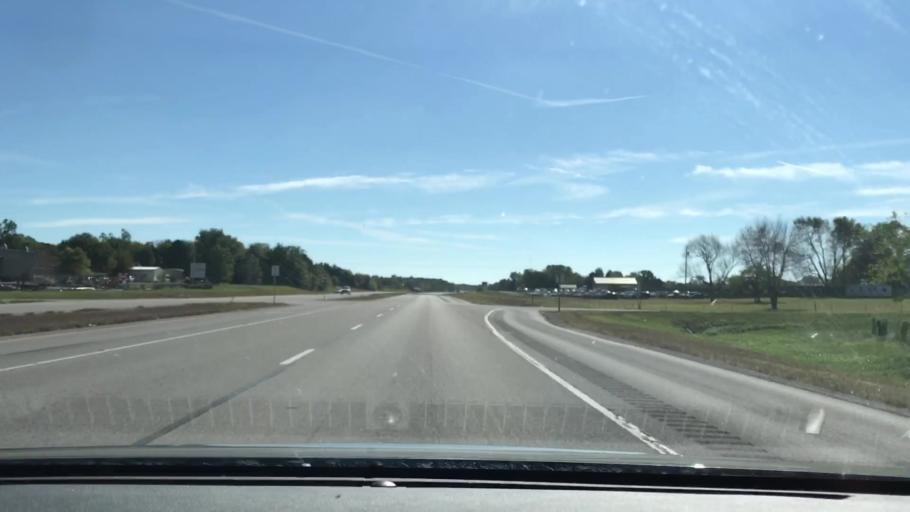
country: US
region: Kentucky
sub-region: Todd County
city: Elkton
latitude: 36.8367
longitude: -87.2388
